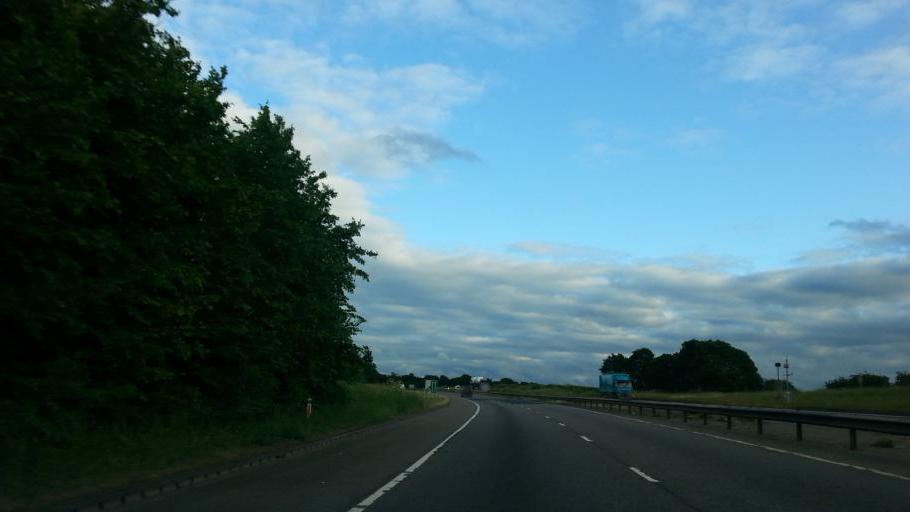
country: GB
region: England
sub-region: Nottinghamshire
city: Bircotes
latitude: 53.3691
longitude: -1.0549
